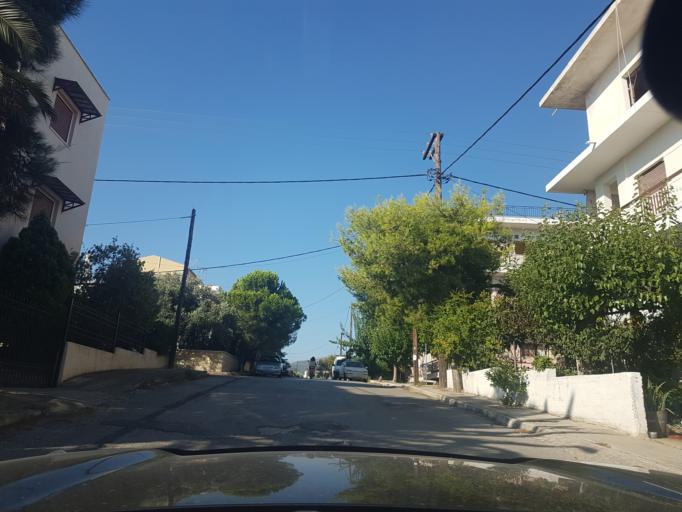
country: GR
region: Central Greece
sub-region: Nomos Evvoias
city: Chalkida
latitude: 38.4739
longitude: 23.5858
